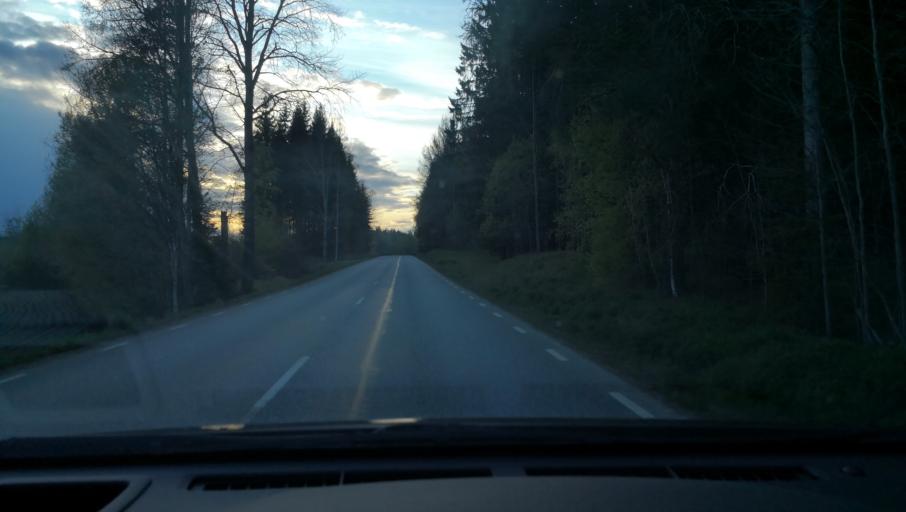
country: SE
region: OErebro
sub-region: Askersunds Kommun
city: Asbro
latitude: 58.9369
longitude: 15.0159
